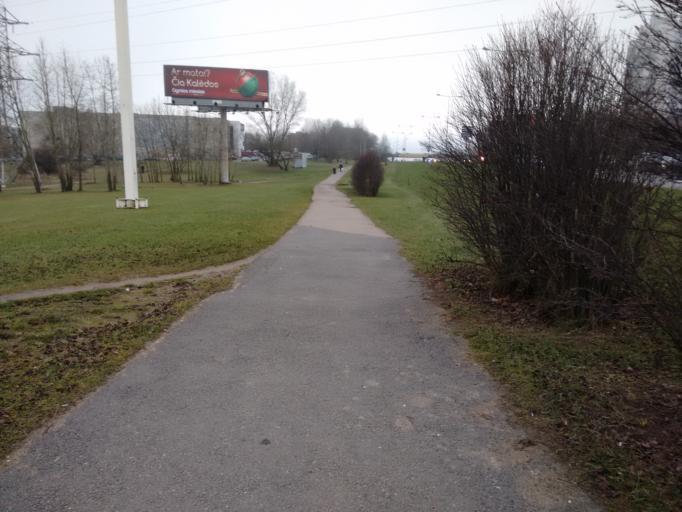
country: LT
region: Vilnius County
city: Seskine
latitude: 54.7199
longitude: 25.2453
